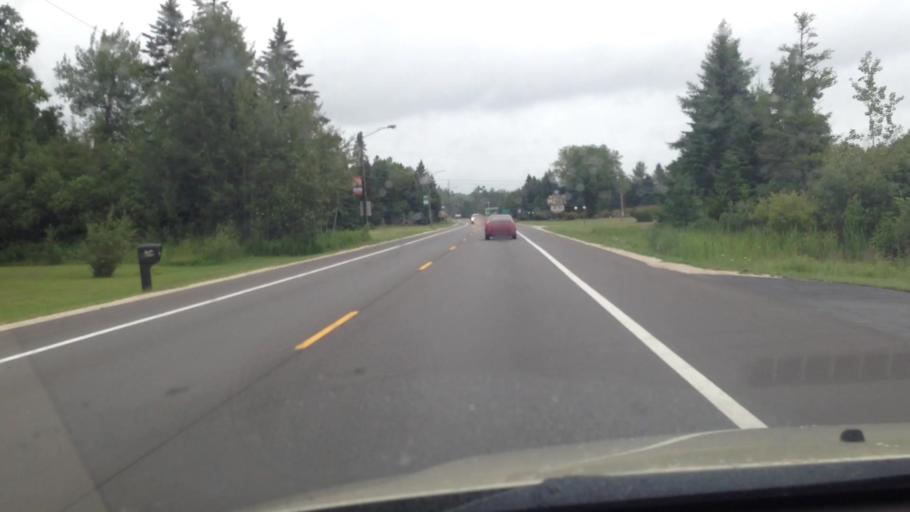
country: US
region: Michigan
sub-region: Schoolcraft County
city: Manistique
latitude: 45.9558
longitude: -86.2251
